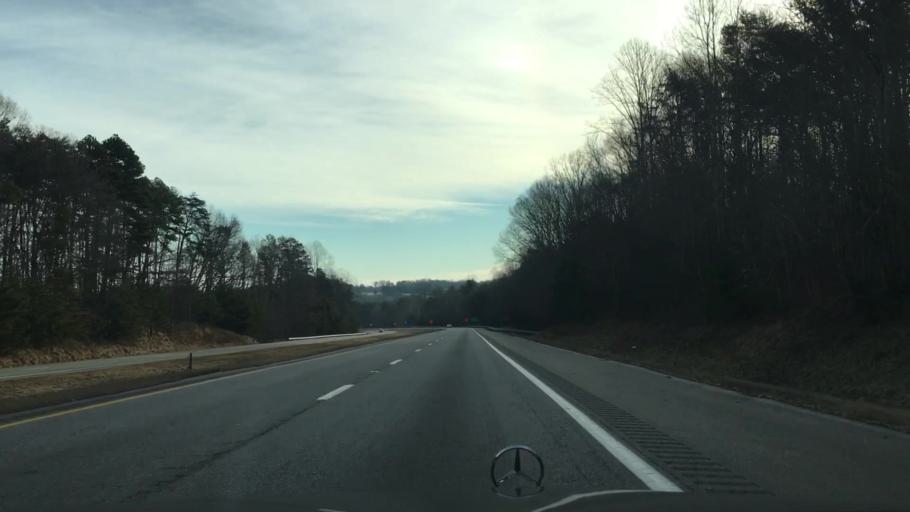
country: US
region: Virginia
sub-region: City of Danville
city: Danville
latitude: 36.5453
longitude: -79.4212
